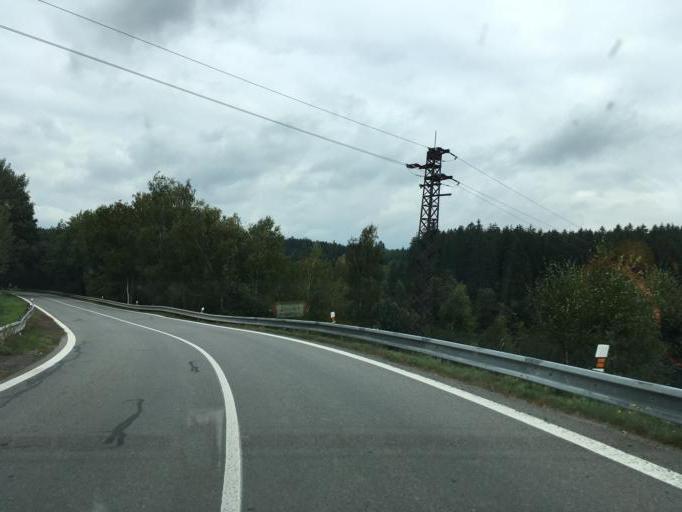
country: CZ
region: Central Bohemia
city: Cechtice
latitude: 49.5764
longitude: 15.0945
